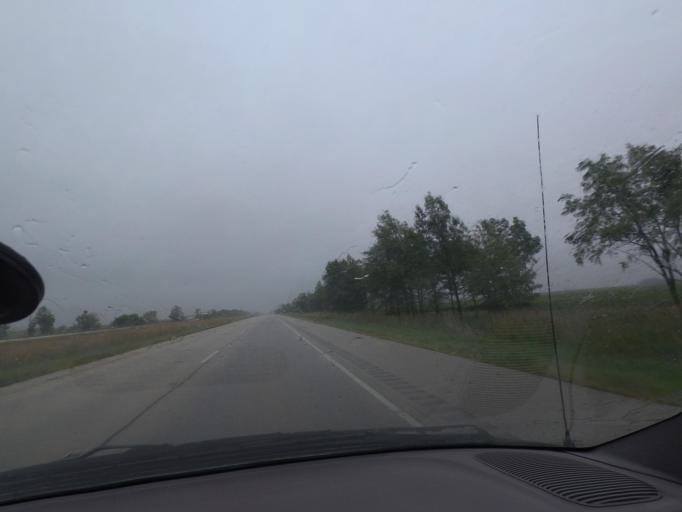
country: US
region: Illinois
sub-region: Sangamon County
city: New Berlin
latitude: 39.7404
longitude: -89.8811
